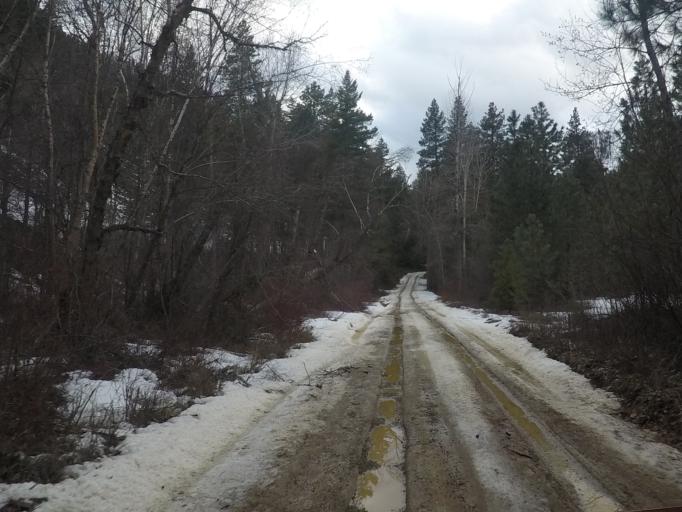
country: US
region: Montana
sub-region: Missoula County
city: Clinton
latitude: 46.5690
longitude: -113.6893
